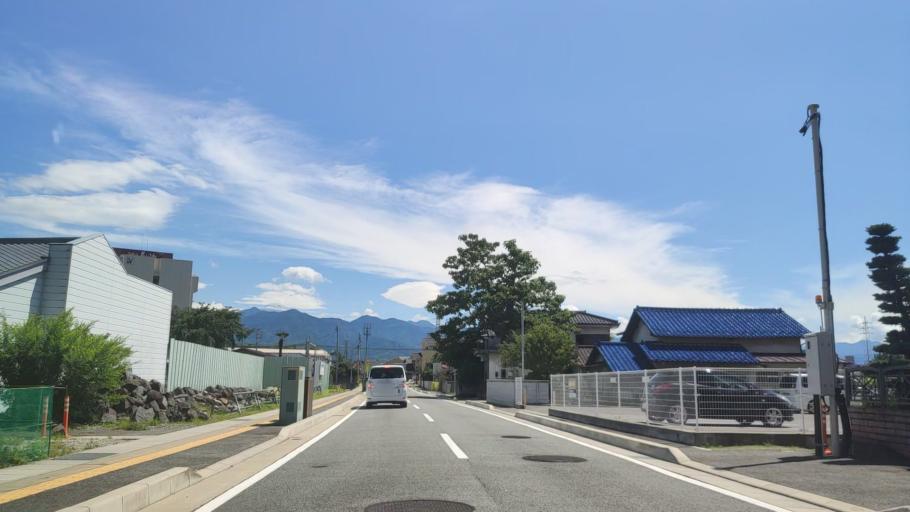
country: JP
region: Yamanashi
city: Isawa
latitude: 35.6592
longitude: 138.6382
